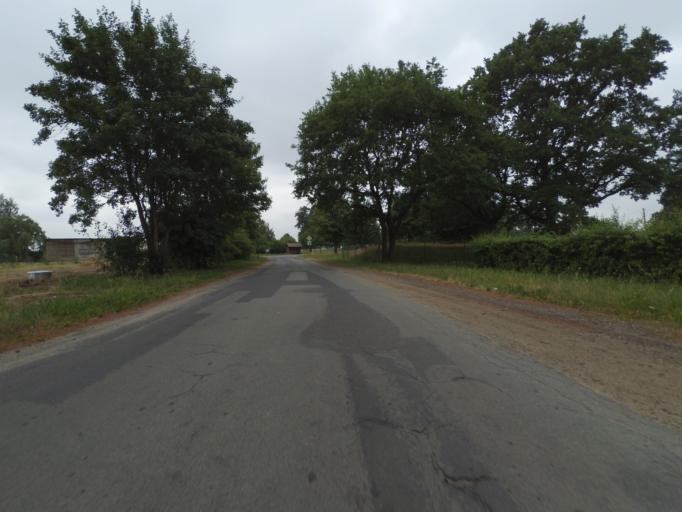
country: DE
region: Mecklenburg-Vorpommern
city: Domsuhl
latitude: 53.4951
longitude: 11.8164
